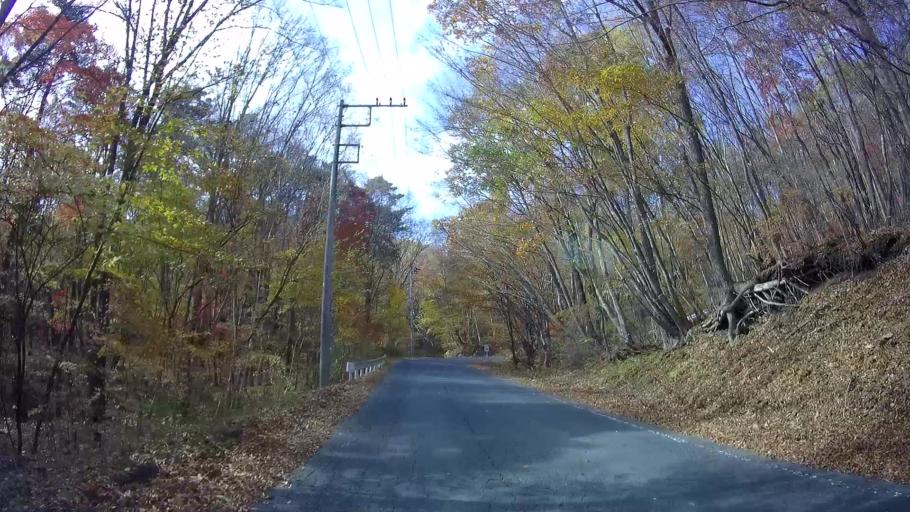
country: JP
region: Gunma
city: Nakanojomachi
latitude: 36.5175
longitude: 138.6670
